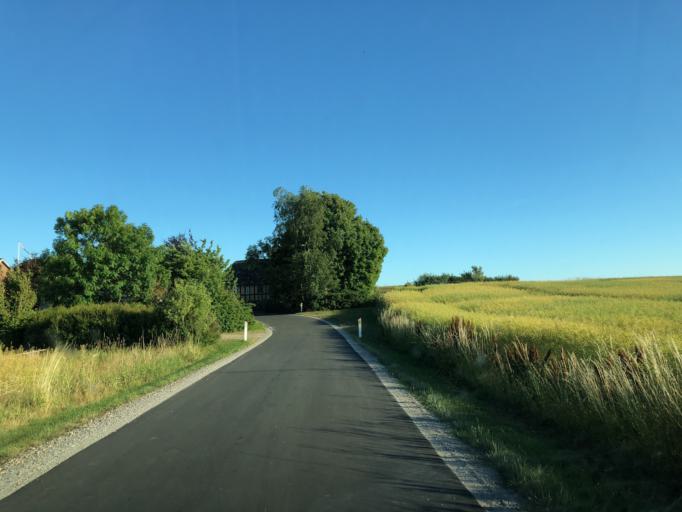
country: DK
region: Central Jutland
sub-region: Horsens Kommune
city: Horsens
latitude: 55.9634
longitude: 9.8199
